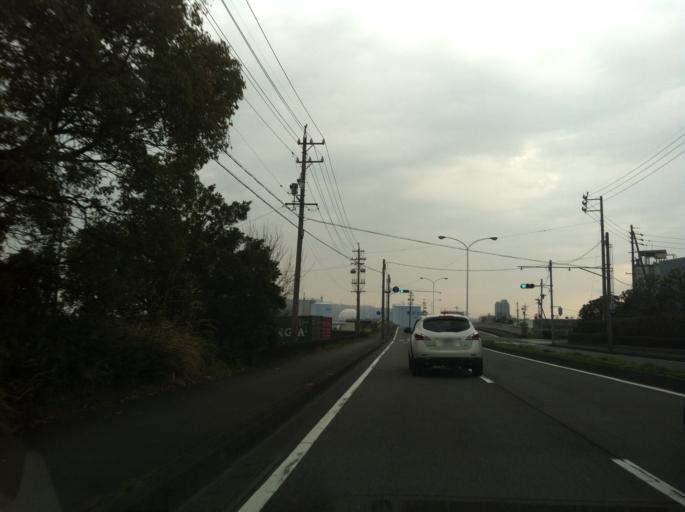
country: JP
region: Shizuoka
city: Shizuoka-shi
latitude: 35.0377
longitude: 138.5012
